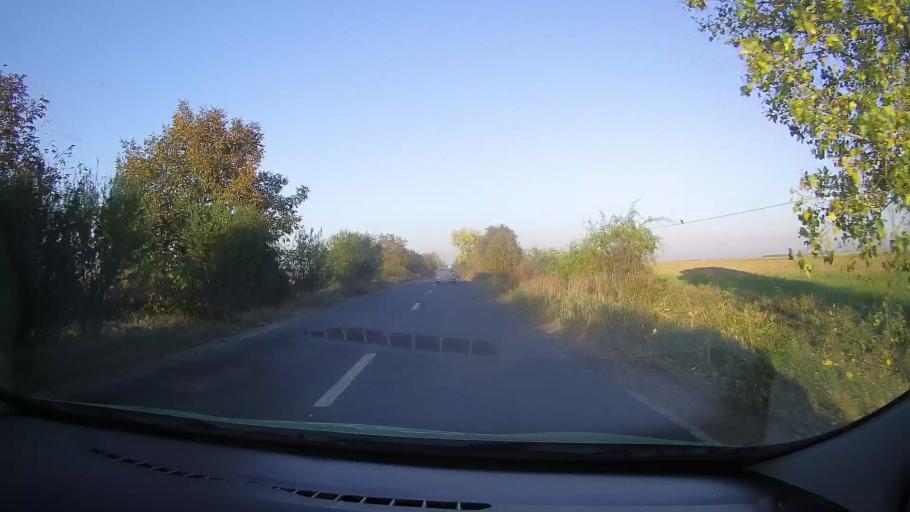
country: RO
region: Bihor
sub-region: Comuna Salard
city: Salard
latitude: 47.1935
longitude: 21.9984
